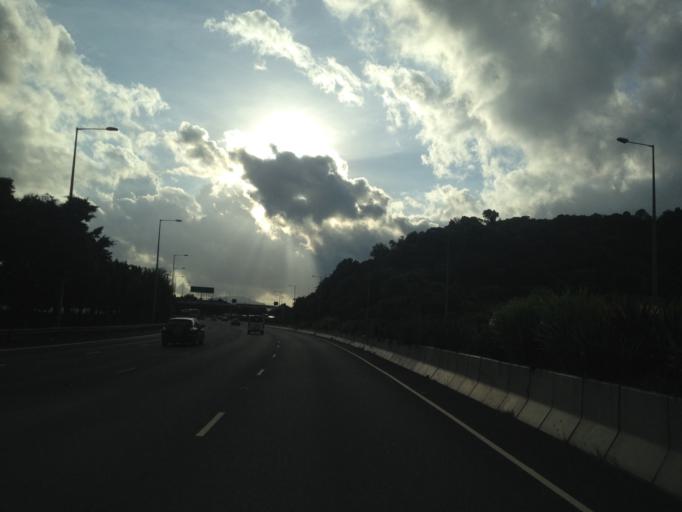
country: HK
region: Tai Po
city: Tai Po
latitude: 22.4391
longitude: 114.1889
